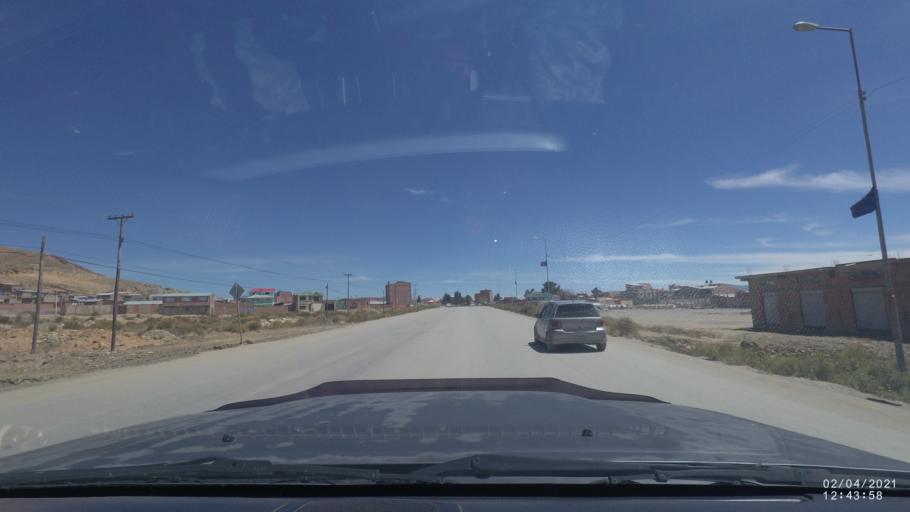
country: BO
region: Oruro
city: Oruro
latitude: -17.9276
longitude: -67.1248
